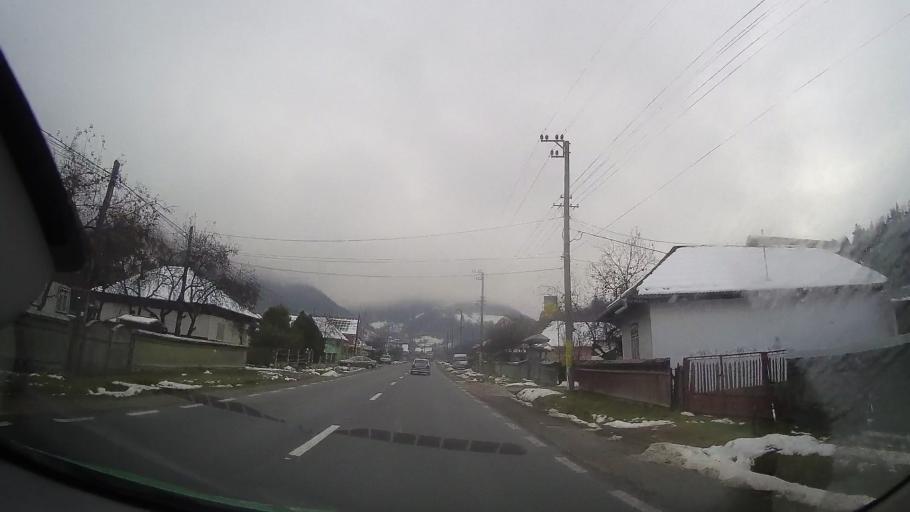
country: RO
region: Neamt
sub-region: Comuna Bicazu Ardelean
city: Bicazu Ardelean
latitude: 46.8600
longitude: 25.9367
